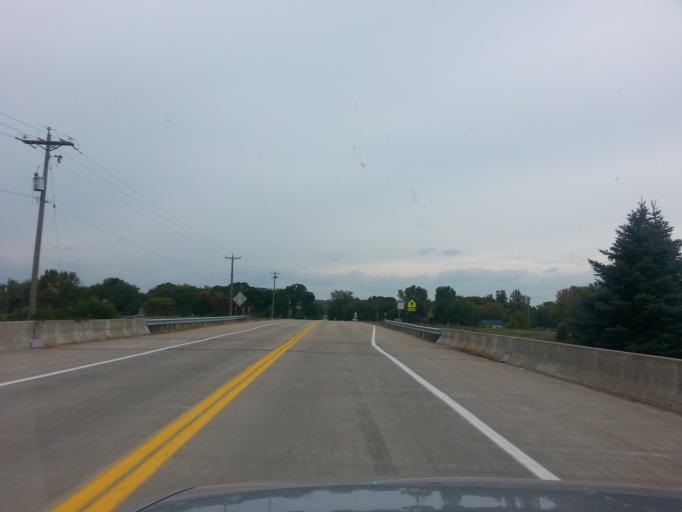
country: US
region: Minnesota
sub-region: Washington County
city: Lake Elmo
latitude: 44.9487
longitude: -92.8428
